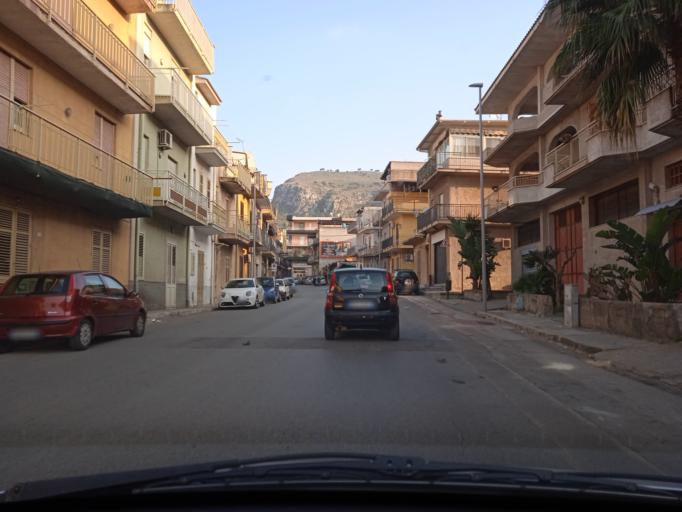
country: IT
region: Sicily
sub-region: Palermo
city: Villabate
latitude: 38.0770
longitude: 13.4391
